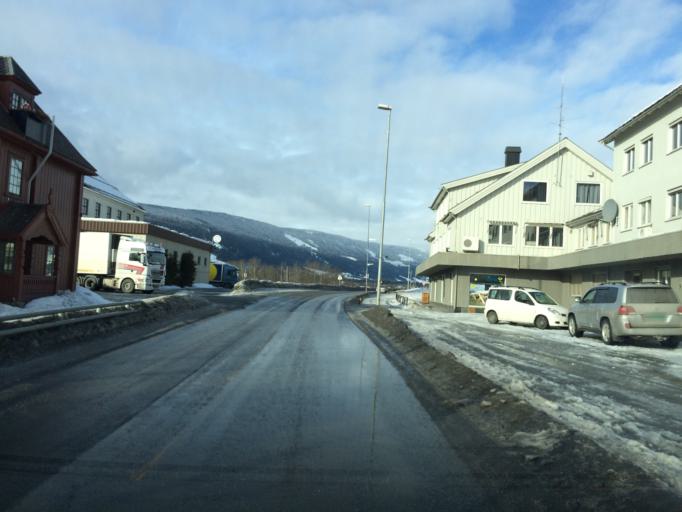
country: NO
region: Oppland
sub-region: Gausdal
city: Segalstad bru
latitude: 61.2285
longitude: 10.2216
